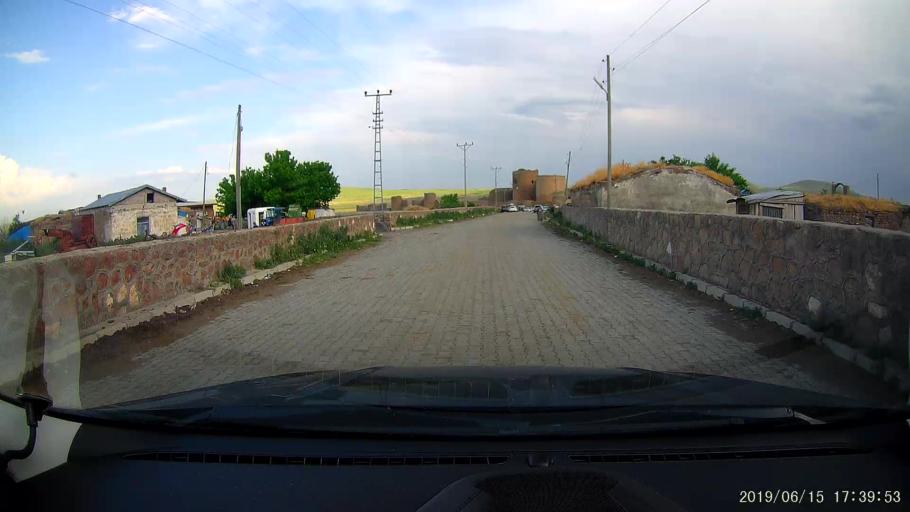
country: TR
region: Kars
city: Basgedikler
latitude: 40.5138
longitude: 43.5716
